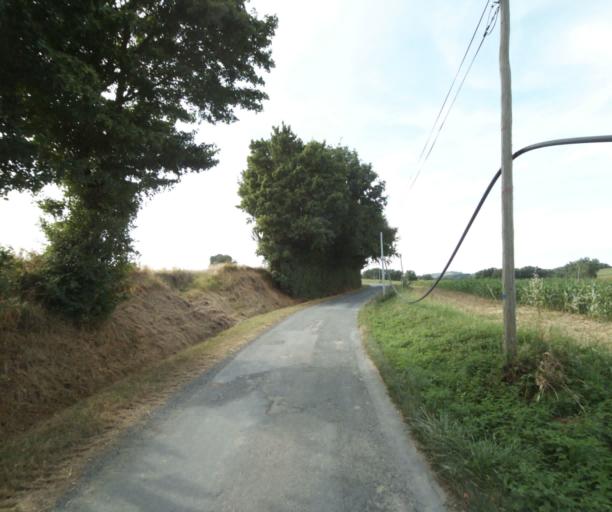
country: FR
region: Midi-Pyrenees
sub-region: Departement du Tarn
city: Soual
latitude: 43.5296
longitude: 2.0595
